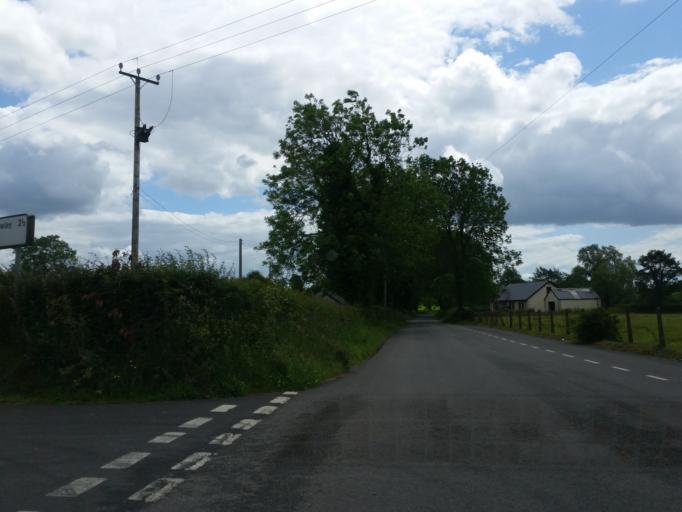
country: GB
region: Northern Ireland
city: Fivemiletown
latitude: 54.4578
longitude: -7.0771
